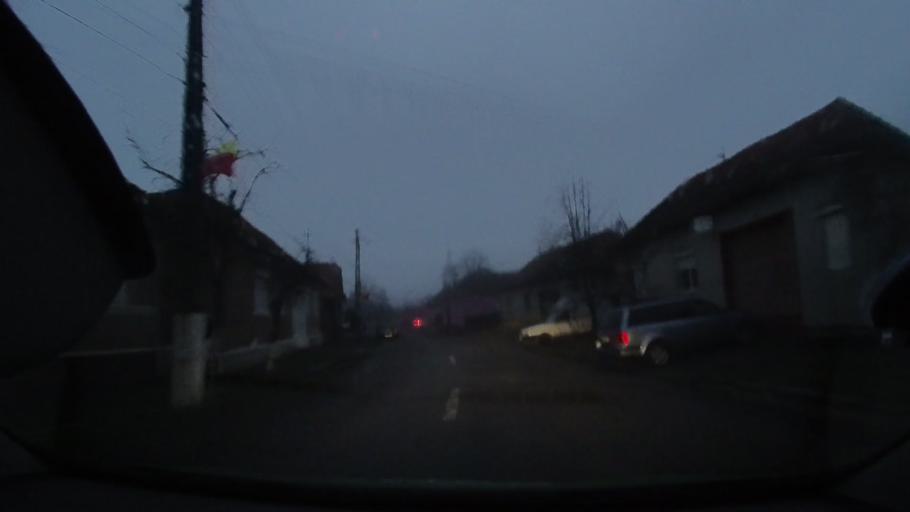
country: RO
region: Arad
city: Hatzmas
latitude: 46.5031
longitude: 22.0776
